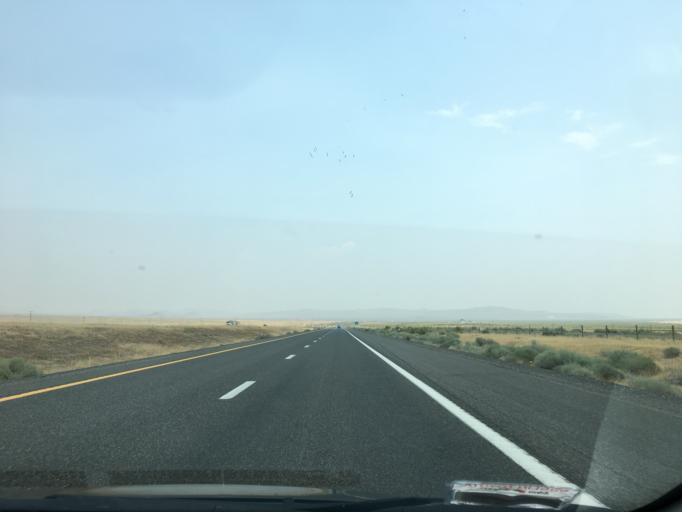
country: US
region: Nevada
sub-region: Pershing County
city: Lovelock
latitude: 40.0415
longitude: -118.6637
